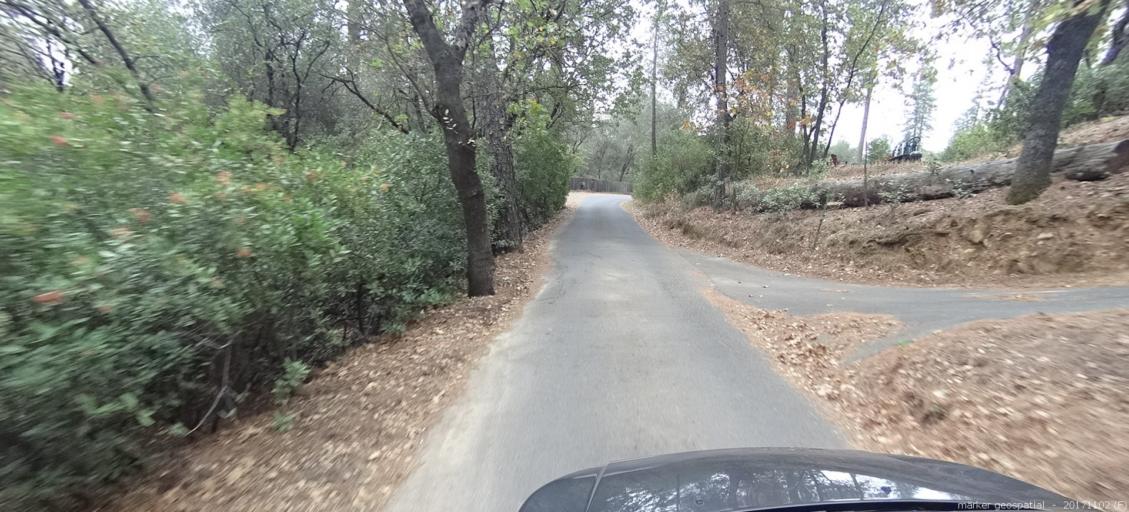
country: US
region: California
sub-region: Shasta County
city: Central Valley (historical)
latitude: 40.6462
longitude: -122.4060
